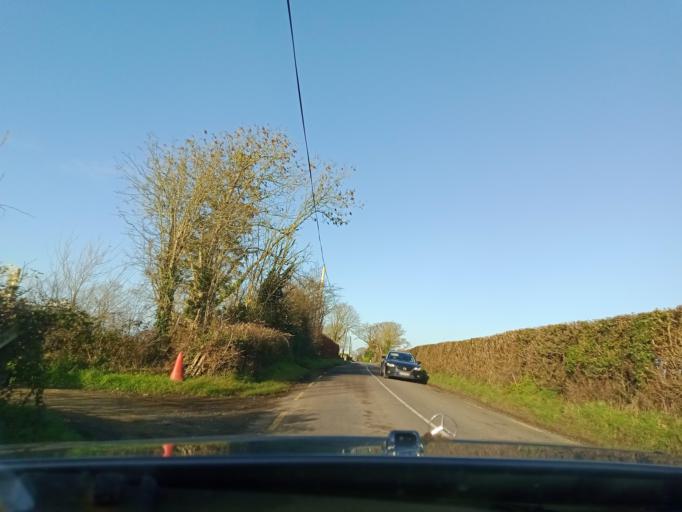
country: IE
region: Leinster
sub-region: Kilkenny
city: Callan
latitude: 52.5083
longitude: -7.3843
